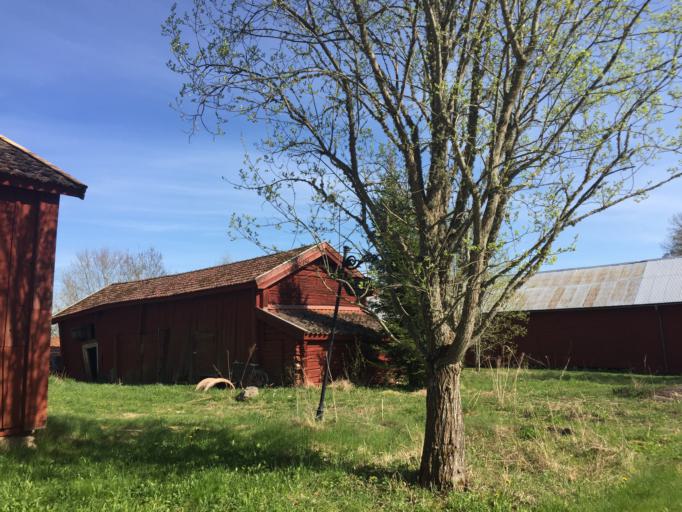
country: SE
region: OErebro
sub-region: Lekebergs Kommun
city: Fjugesta
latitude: 59.1798
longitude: 14.9283
